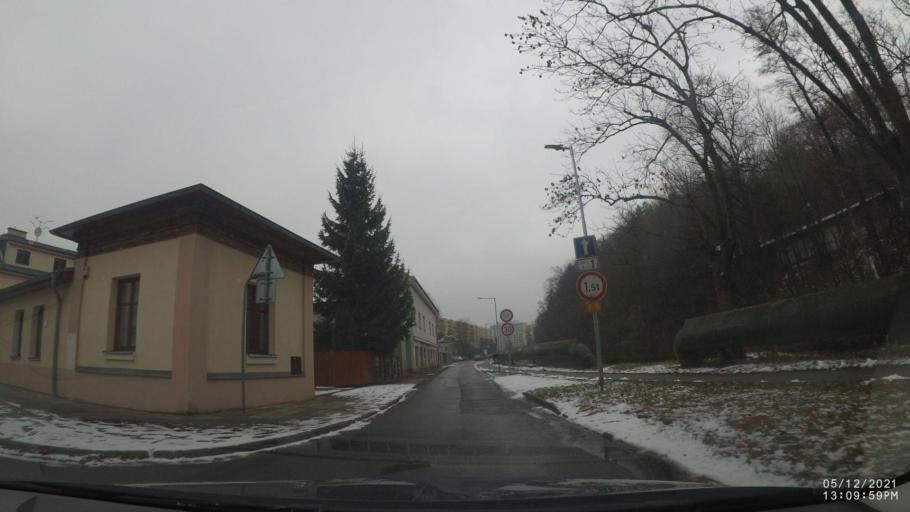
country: CZ
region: Kralovehradecky
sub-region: Okres Nachod
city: Nachod
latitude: 50.4157
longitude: 16.1713
